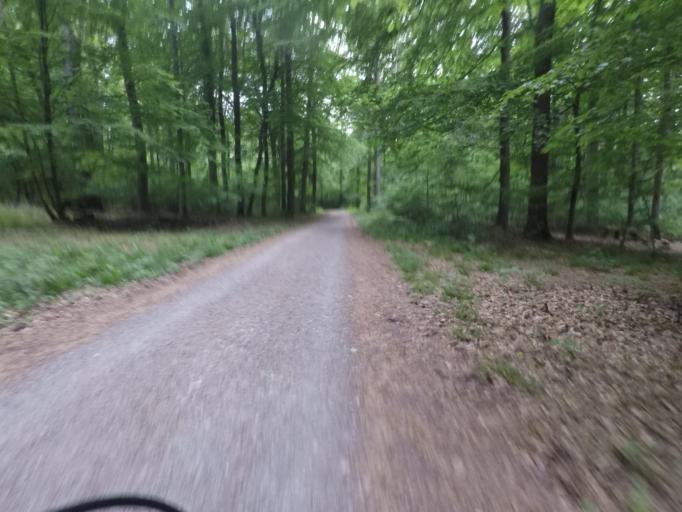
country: DE
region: North Rhine-Westphalia
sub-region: Regierungsbezirk Detmold
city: Bad Salzuflen
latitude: 52.1109
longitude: 8.7406
